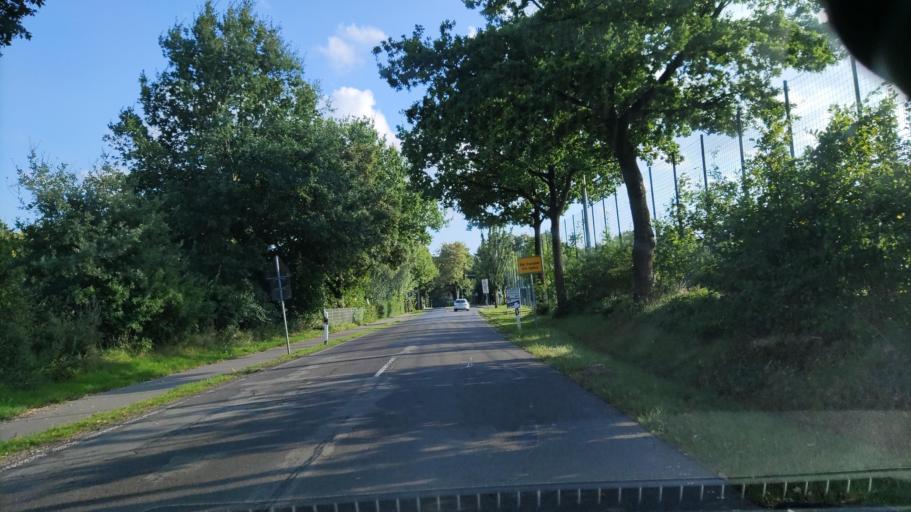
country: DE
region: Schleswig-Holstein
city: Bad Bramstedt
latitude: 53.9278
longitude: 9.8717
